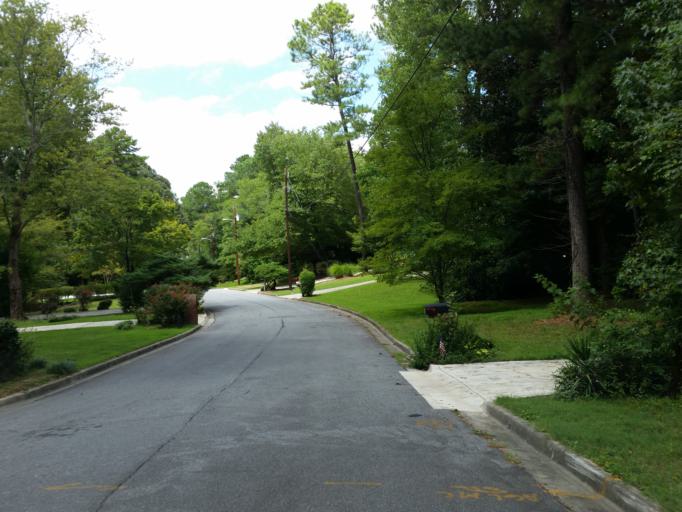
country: US
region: Georgia
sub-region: Cobb County
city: Smyrna
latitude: 33.9443
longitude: -84.4723
